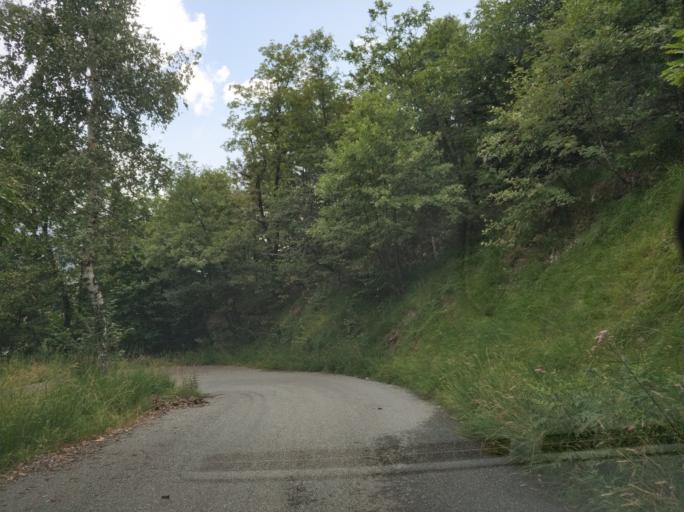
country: IT
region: Piedmont
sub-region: Provincia di Torino
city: Viu
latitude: 45.2261
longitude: 7.3935
